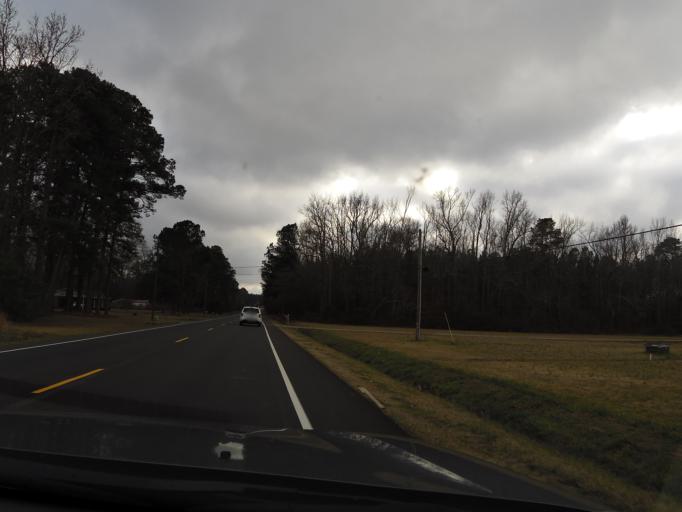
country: US
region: North Carolina
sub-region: Nash County
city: Rocky Mount
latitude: 35.9017
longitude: -77.7402
